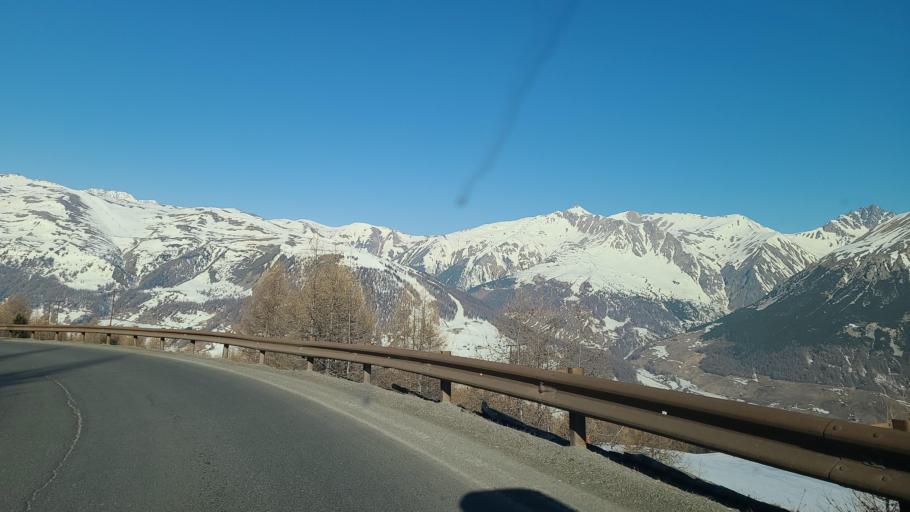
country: IT
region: Lombardy
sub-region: Provincia di Sondrio
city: Livigno
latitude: 46.5382
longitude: 10.1605
